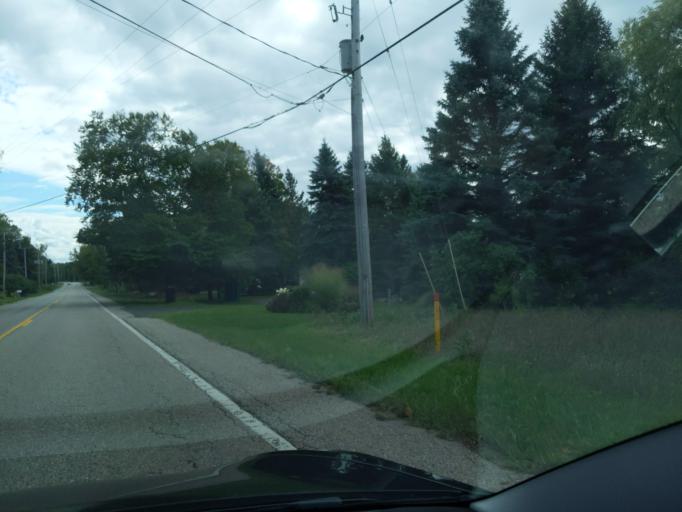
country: US
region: Michigan
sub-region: Kalkaska County
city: Rapid City
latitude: 44.9124
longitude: -85.2838
